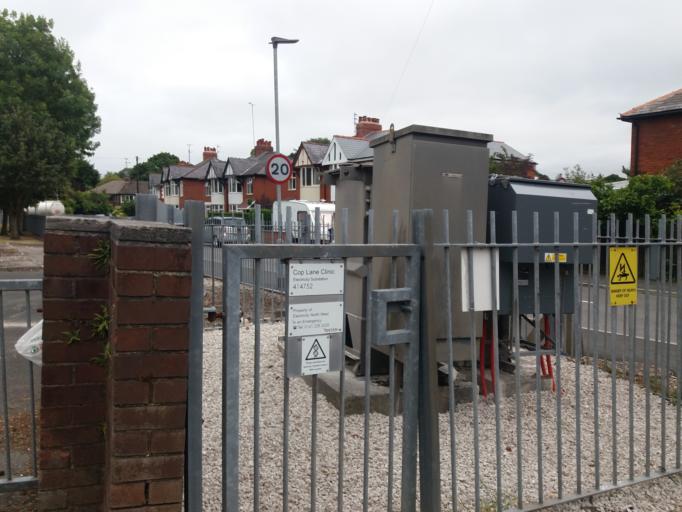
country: GB
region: England
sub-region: Lancashire
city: Preston
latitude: 53.7464
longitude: -2.7292
